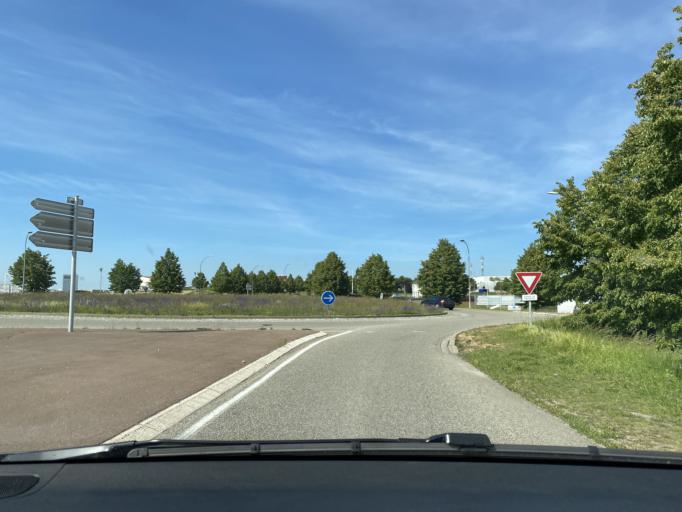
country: FR
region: Lorraine
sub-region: Departement de la Moselle
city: OEting
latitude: 49.1637
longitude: 6.9186
